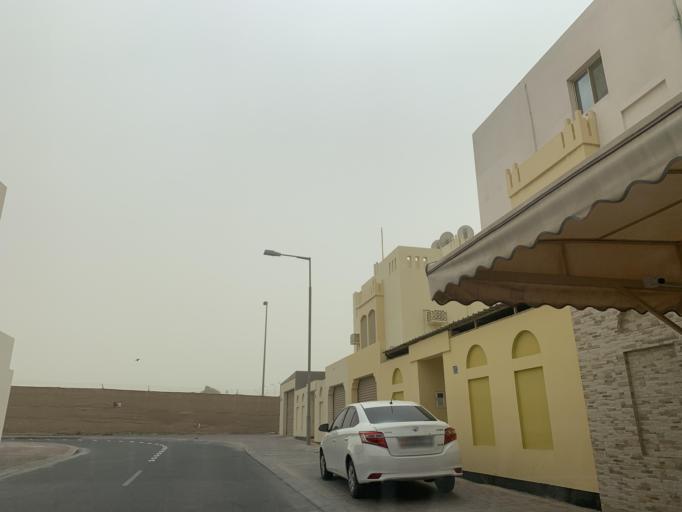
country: BH
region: Central Governorate
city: Madinat Hamad
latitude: 26.1279
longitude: 50.5130
